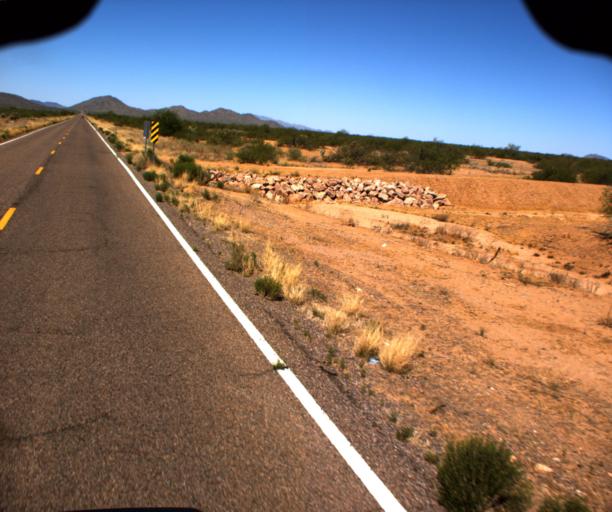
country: US
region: Arizona
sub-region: Yavapai County
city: Congress
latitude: 34.1317
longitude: -112.9298
